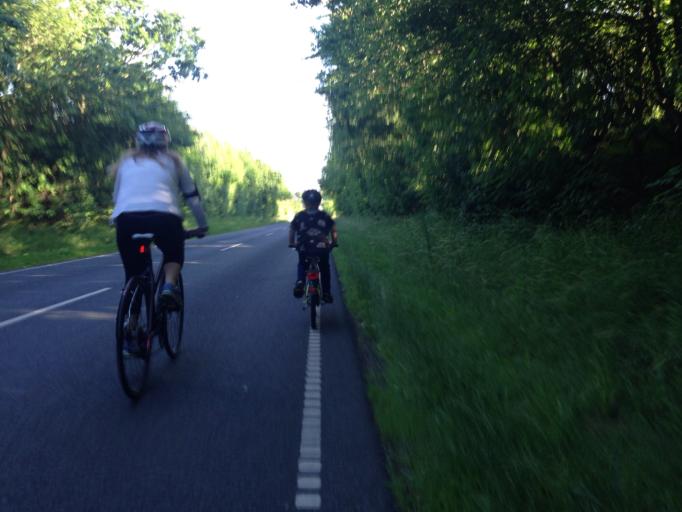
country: DK
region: South Denmark
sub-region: Middelfart Kommune
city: Norre Aby
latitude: 55.4877
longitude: 9.9024
